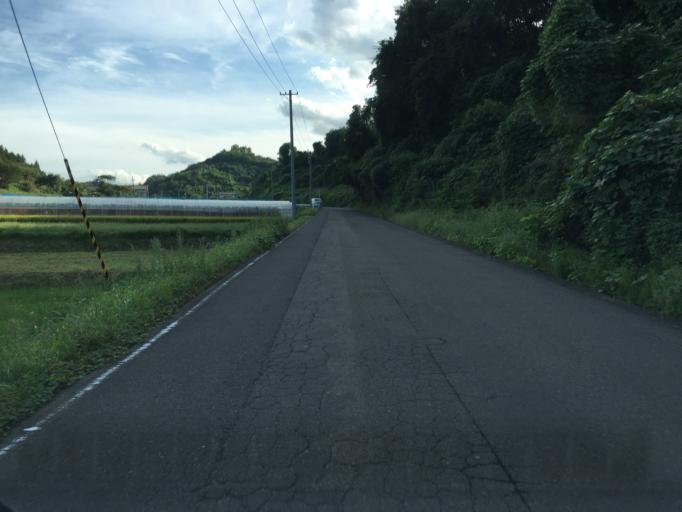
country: JP
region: Fukushima
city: Yanagawamachi-saiwaicho
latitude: 37.8126
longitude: 140.5889
